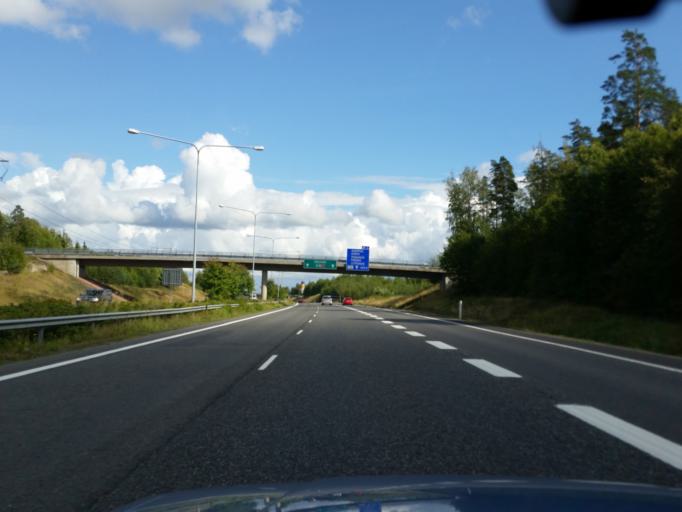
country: FI
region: Varsinais-Suomi
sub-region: Turku
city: Kaarina
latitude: 60.4219
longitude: 22.3588
